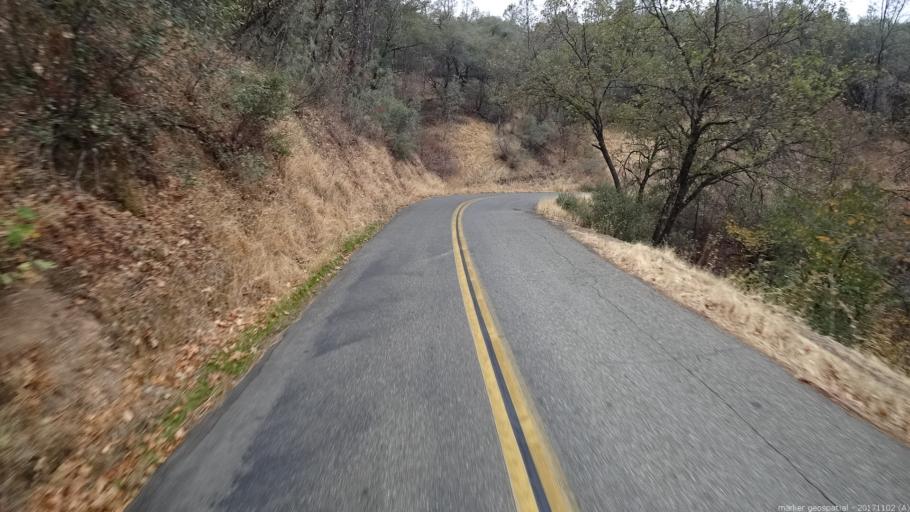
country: US
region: California
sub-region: Shasta County
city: Bella Vista
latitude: 40.7320
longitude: -122.2402
